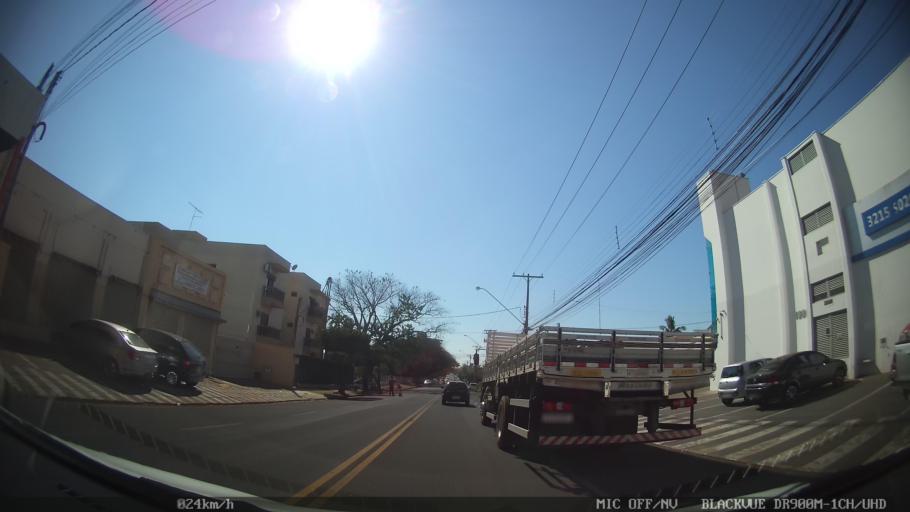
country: BR
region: Sao Paulo
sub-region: Sao Jose Do Rio Preto
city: Sao Jose do Rio Preto
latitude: -20.7993
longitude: -49.3951
